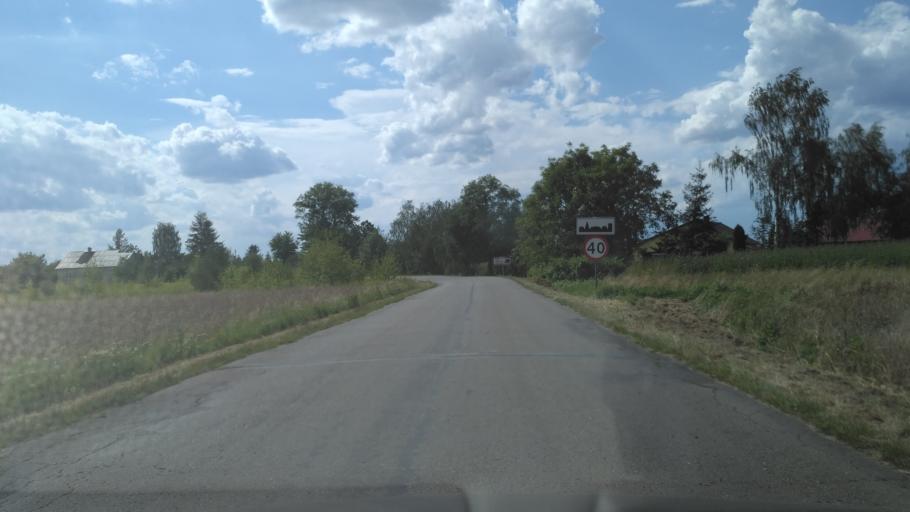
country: PL
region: Lublin Voivodeship
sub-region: Powiat leczynski
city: Milejow
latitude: 51.2174
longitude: 22.9007
